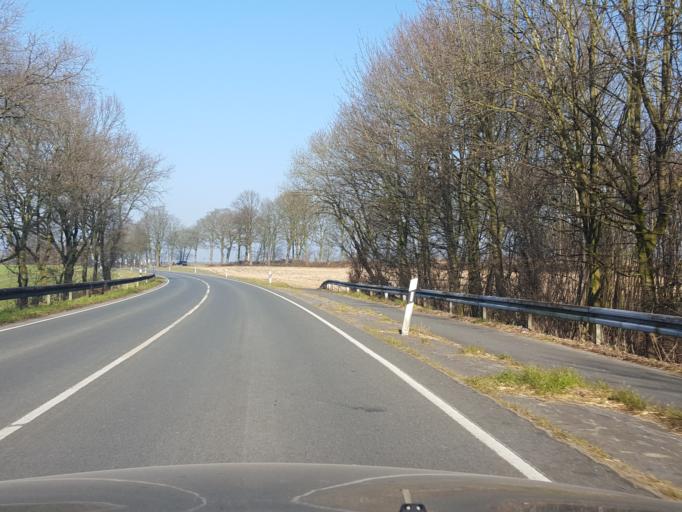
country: DE
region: North Rhine-Westphalia
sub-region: Regierungsbezirk Munster
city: Recklinghausen
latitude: 51.6612
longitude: 7.2143
